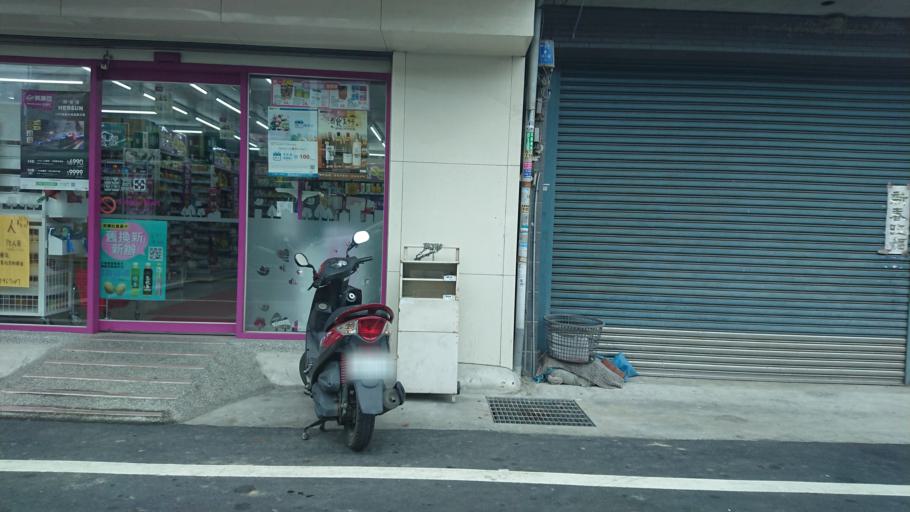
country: TW
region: Taiwan
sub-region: Hsinchu
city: Hsinchu
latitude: 24.8419
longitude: 120.9549
